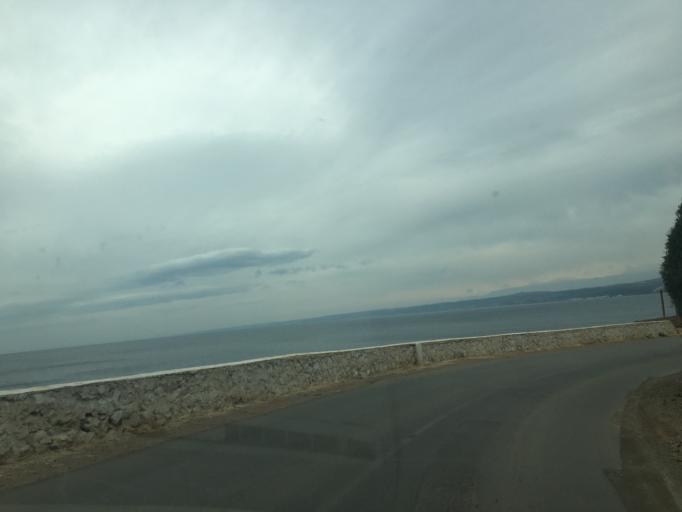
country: DZ
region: Tipaza
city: Tipasa
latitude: 36.6239
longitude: 2.4073
